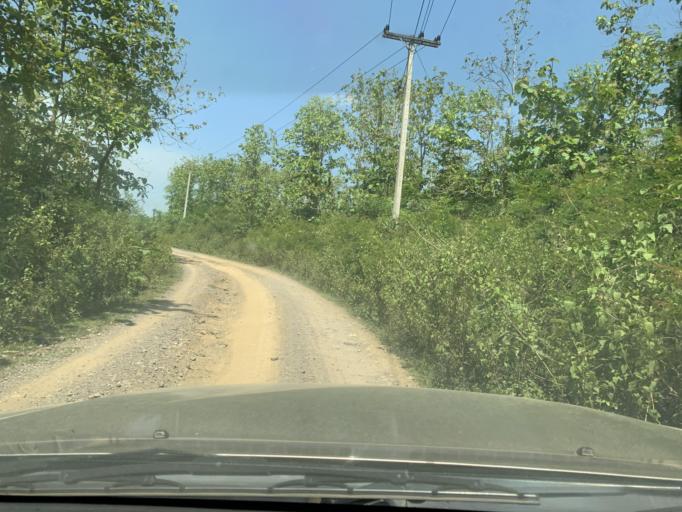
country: LA
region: Louangphabang
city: Louangphabang
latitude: 19.9149
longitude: 102.2666
